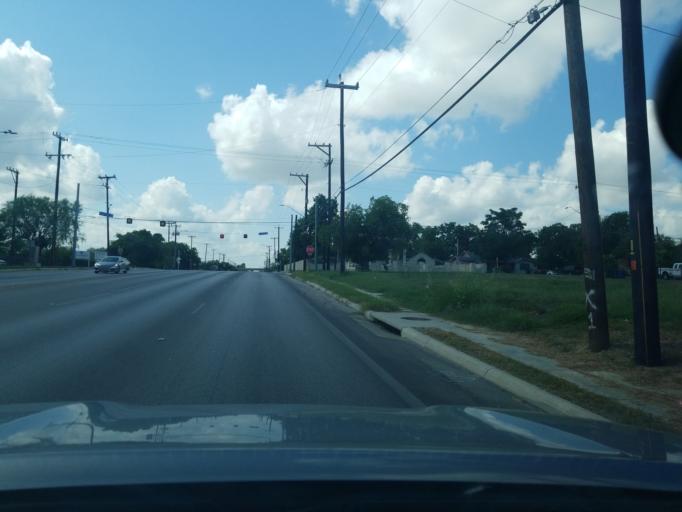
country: US
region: Texas
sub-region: Bexar County
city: Lackland Air Force Base
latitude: 29.3262
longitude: -98.5327
